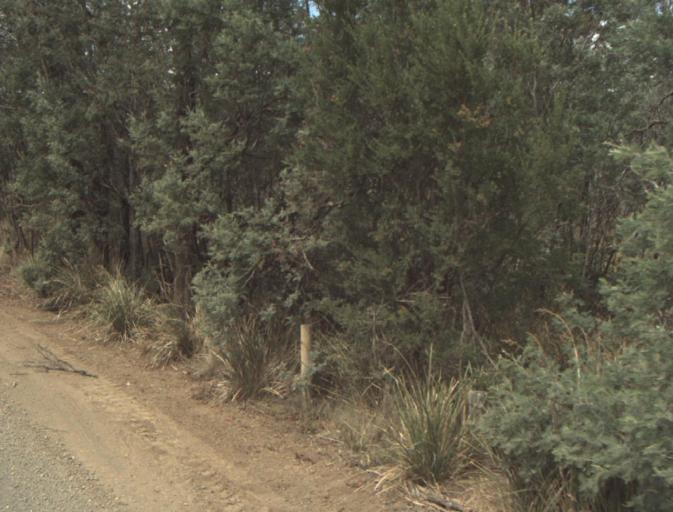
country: AU
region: Tasmania
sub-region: Northern Midlands
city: Evandale
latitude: -41.5131
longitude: 147.3483
